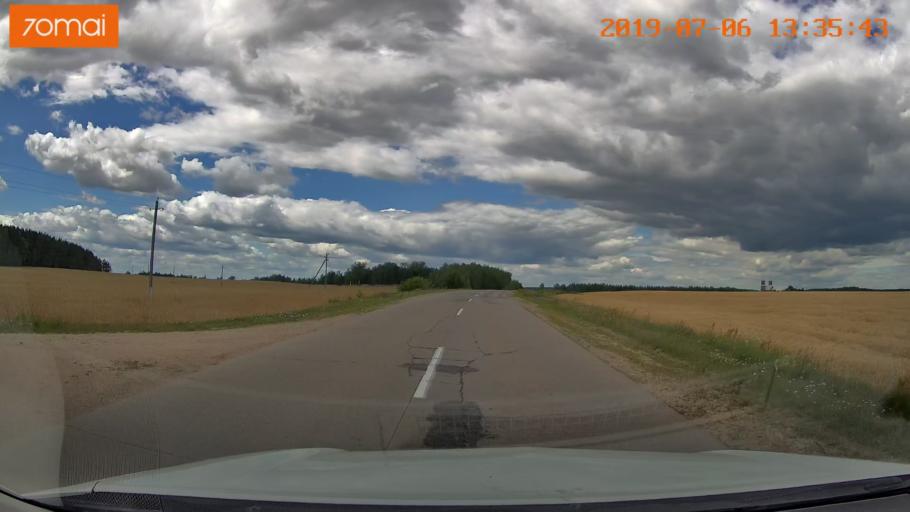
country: BY
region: Minsk
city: Enyerhyetykaw
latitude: 53.6842
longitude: 26.8751
